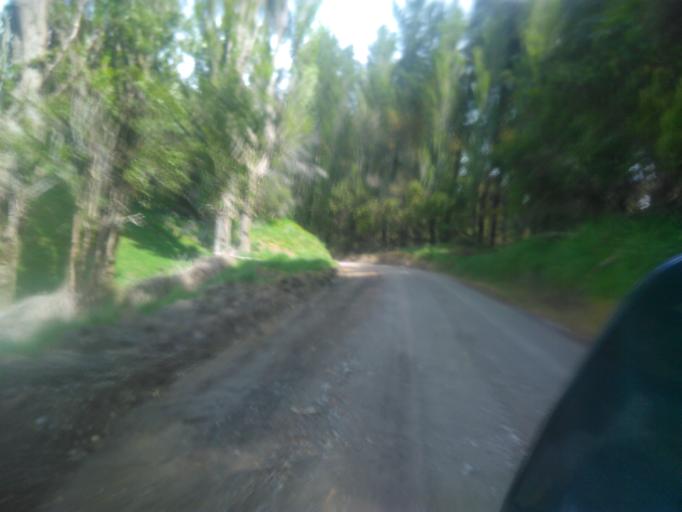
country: NZ
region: Hawke's Bay
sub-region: Wairoa District
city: Wairoa
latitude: -38.7696
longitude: 177.5964
